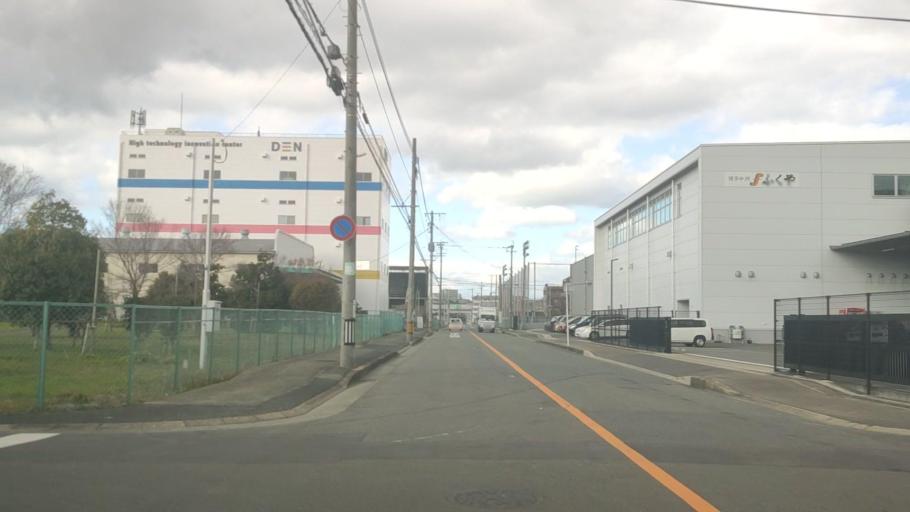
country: JP
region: Fukuoka
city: Fukuoka-shi
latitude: 33.6097
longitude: 130.4348
